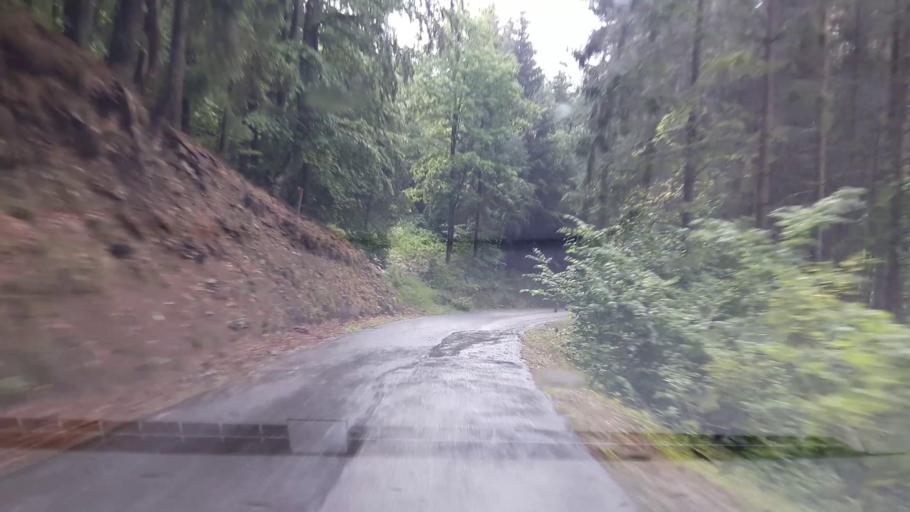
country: AT
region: Lower Austria
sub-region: Politischer Bezirk Krems
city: Aggsbach
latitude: 48.2875
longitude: 15.3782
